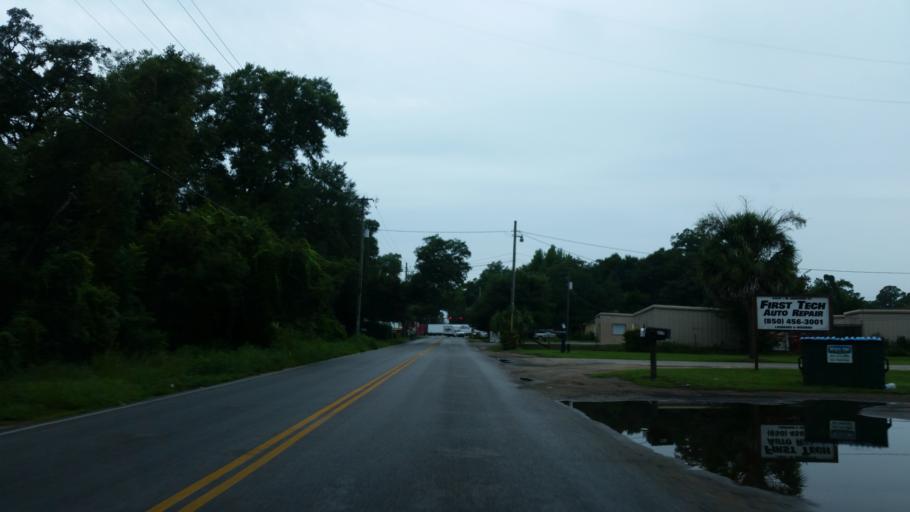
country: US
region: Florida
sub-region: Escambia County
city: West Pensacola
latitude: 30.4183
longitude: -87.2733
